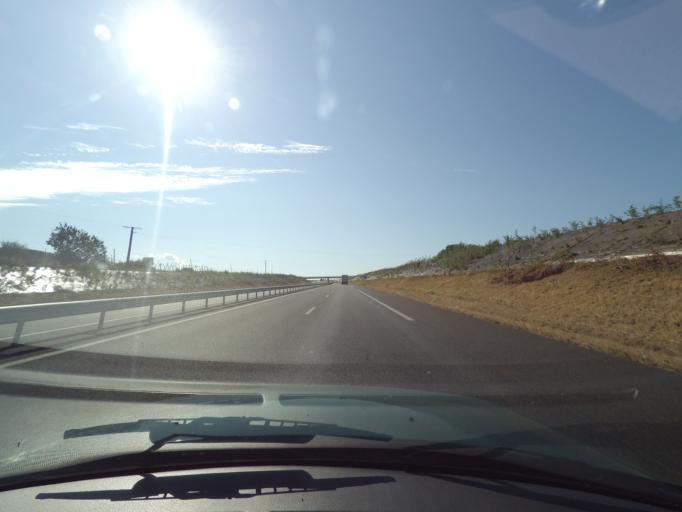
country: FR
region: Poitou-Charentes
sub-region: Departement de la Vienne
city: Savigny-Levescault
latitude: 46.4904
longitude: 0.4998
